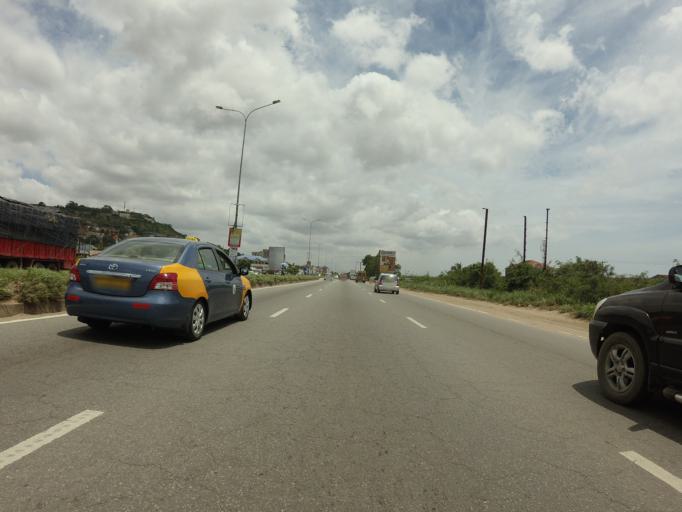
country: GH
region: Greater Accra
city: Gbawe
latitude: 5.5548
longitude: -0.3066
